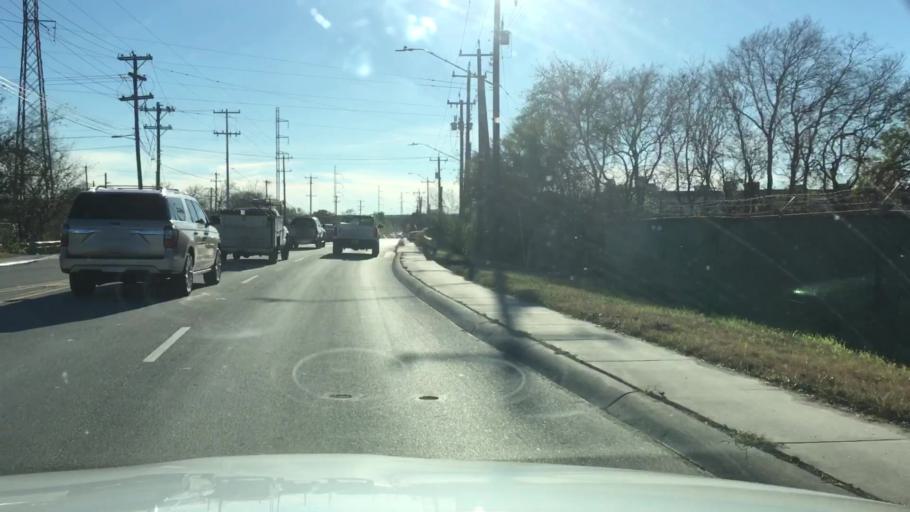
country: US
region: Texas
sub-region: Bexar County
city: Windcrest
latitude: 29.5399
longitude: -98.4222
